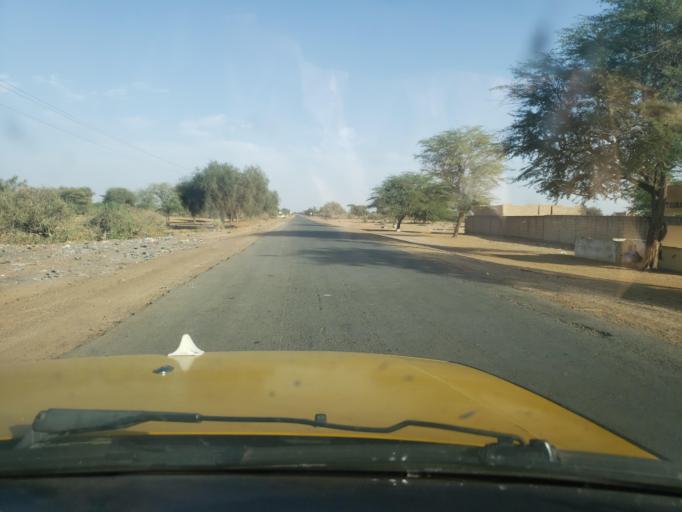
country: SN
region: Louga
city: Louga
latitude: 15.5013
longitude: -15.9395
